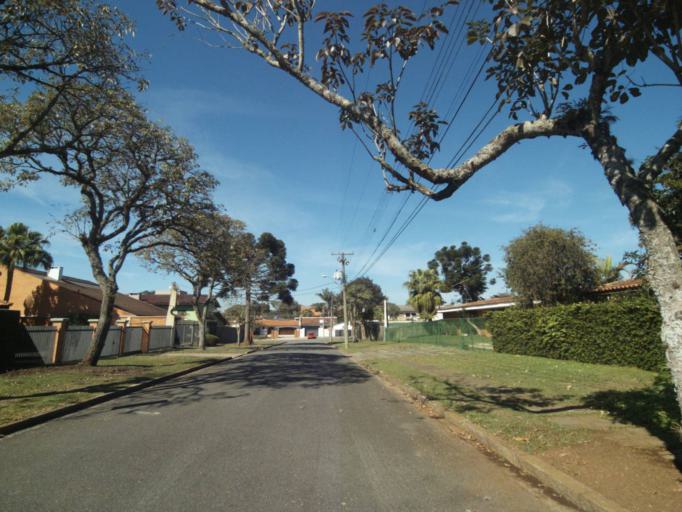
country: BR
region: Parana
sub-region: Curitiba
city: Curitiba
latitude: -25.4139
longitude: -49.2370
